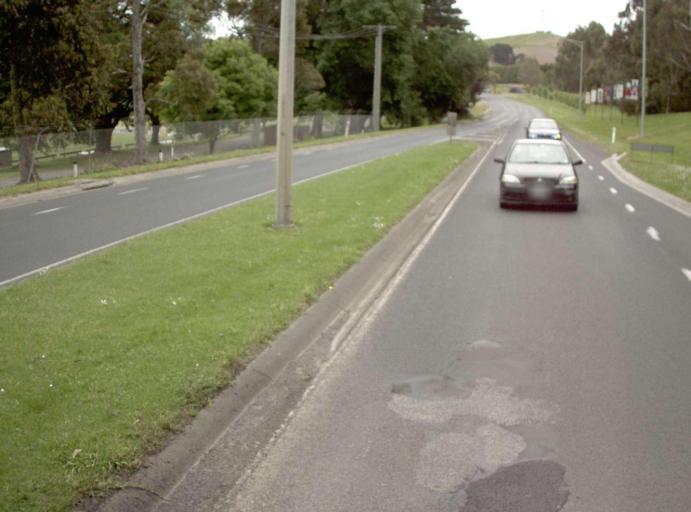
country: AU
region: Victoria
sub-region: Bass Coast
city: North Wonthaggi
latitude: -38.4278
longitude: 145.8202
